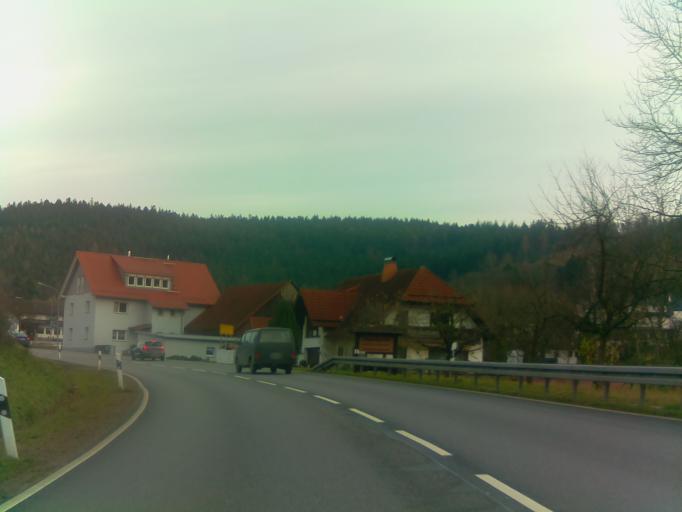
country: DE
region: Hesse
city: Reichelsheim
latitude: 49.6598
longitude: 8.8379
